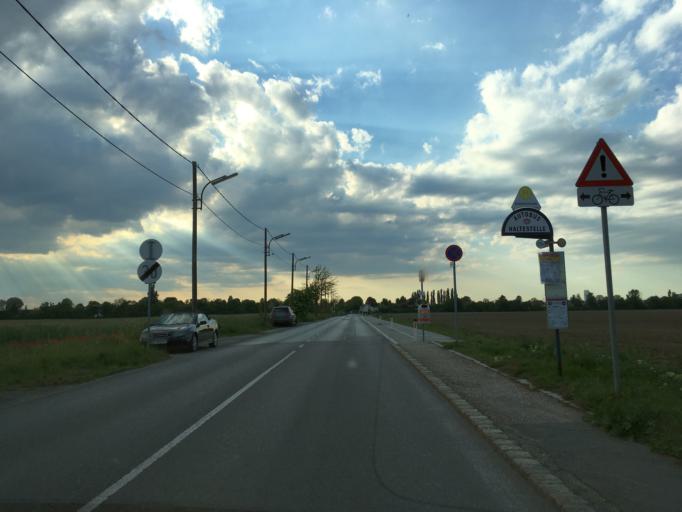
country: AT
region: Lower Austria
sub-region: Politischer Bezirk Wien-Umgebung
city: Gerasdorf bei Wien
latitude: 48.2795
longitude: 16.4921
